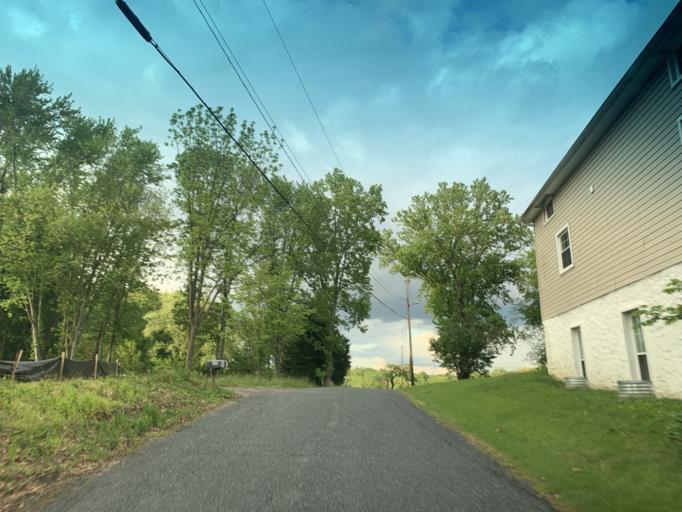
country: US
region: Pennsylvania
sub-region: York County
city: Susquehanna Trails
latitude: 39.7059
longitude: -76.2589
